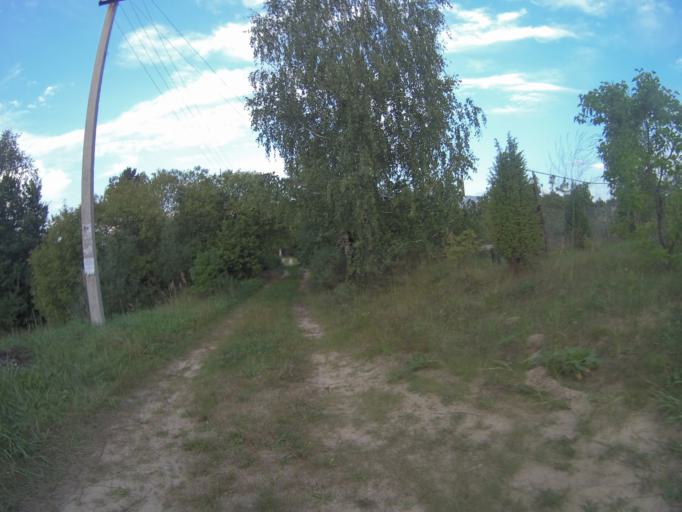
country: RU
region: Vladimir
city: Raduzhnyy
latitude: 56.0248
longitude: 40.2238
